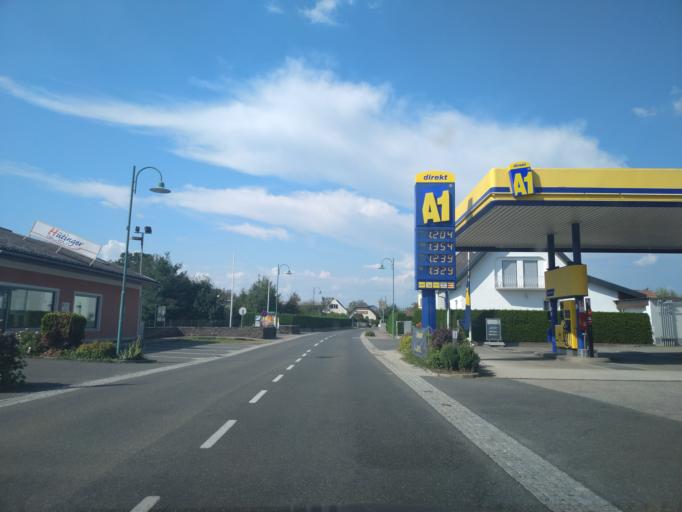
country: AT
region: Styria
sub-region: Politischer Bezirk Leibnitz
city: Kaindorf an der Sulm
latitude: 46.7939
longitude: 15.5383
